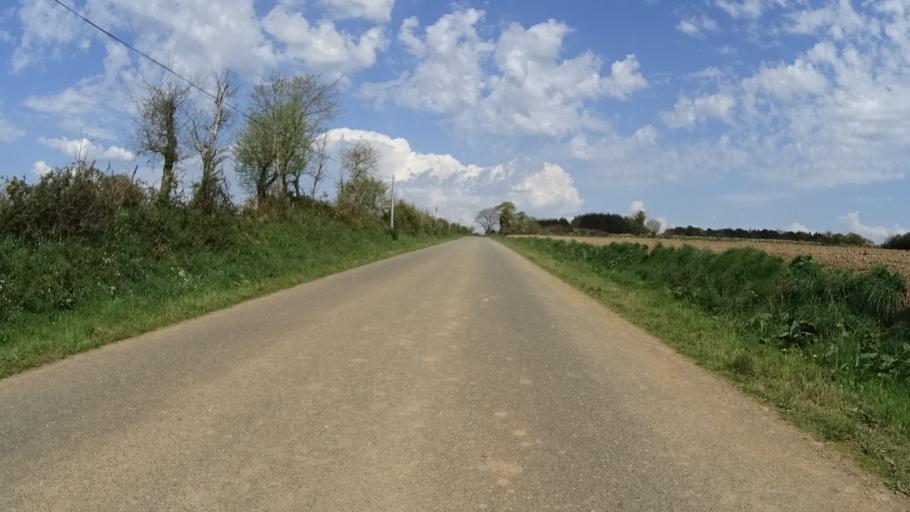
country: FR
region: Brittany
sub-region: Departement du Finistere
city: Sizun
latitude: 48.4278
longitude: -4.0779
